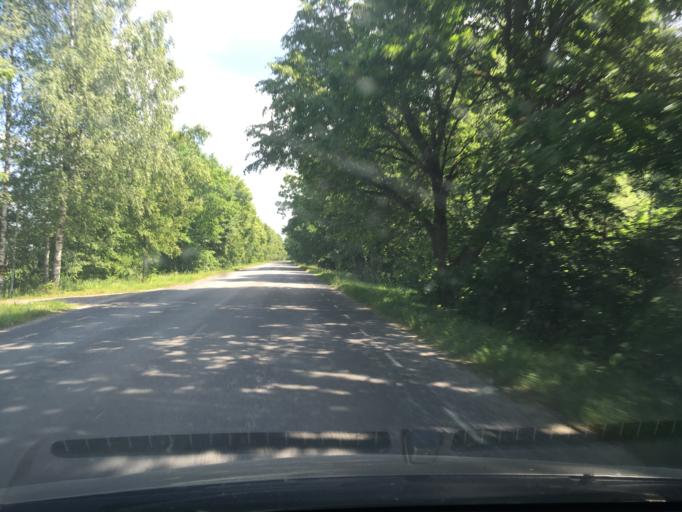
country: EE
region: Paernumaa
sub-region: Halinga vald
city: Parnu-Jaagupi
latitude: 58.7114
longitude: 24.3765
